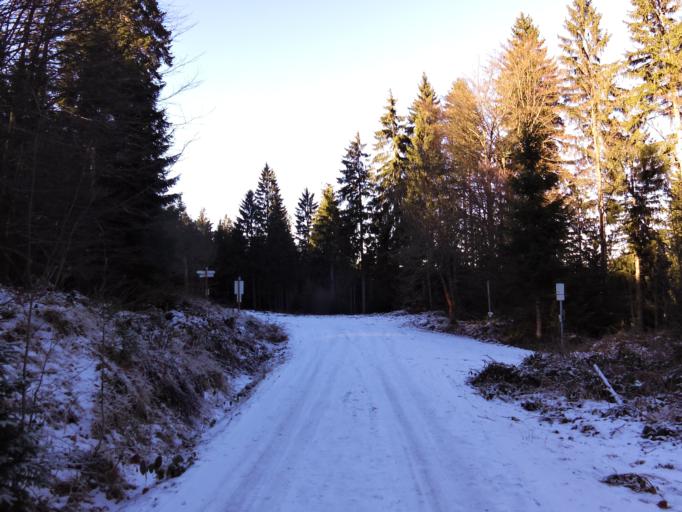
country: DE
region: Bavaria
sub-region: Upper Franconia
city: Fichtelberg
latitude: 50.0362
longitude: 11.8333
